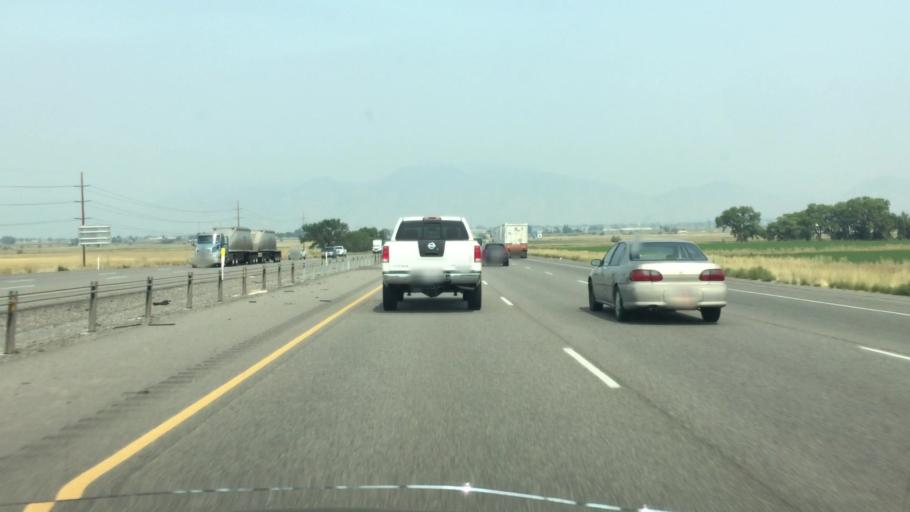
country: US
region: Utah
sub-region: Utah County
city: Payson
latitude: 40.0611
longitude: -111.7273
